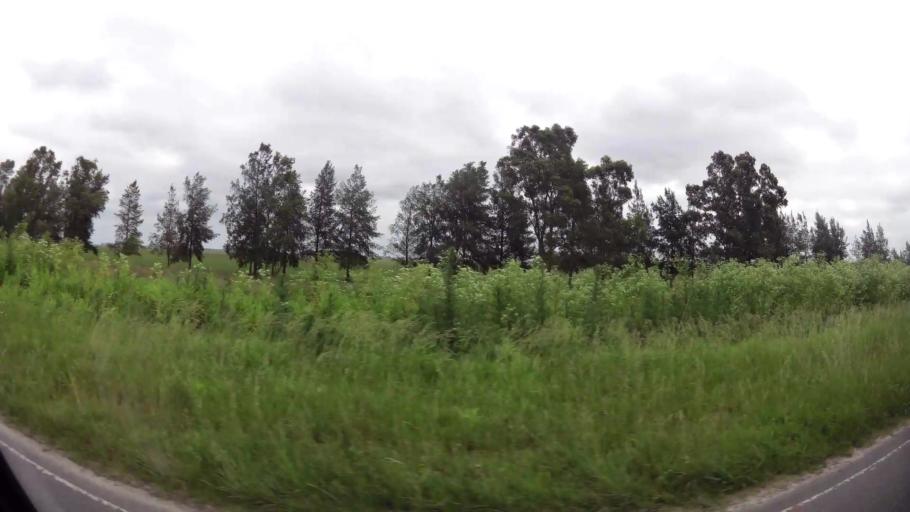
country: AR
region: Buenos Aires
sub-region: Partido de San Vicente
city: San Vicente
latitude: -35.0402
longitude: -58.4542
